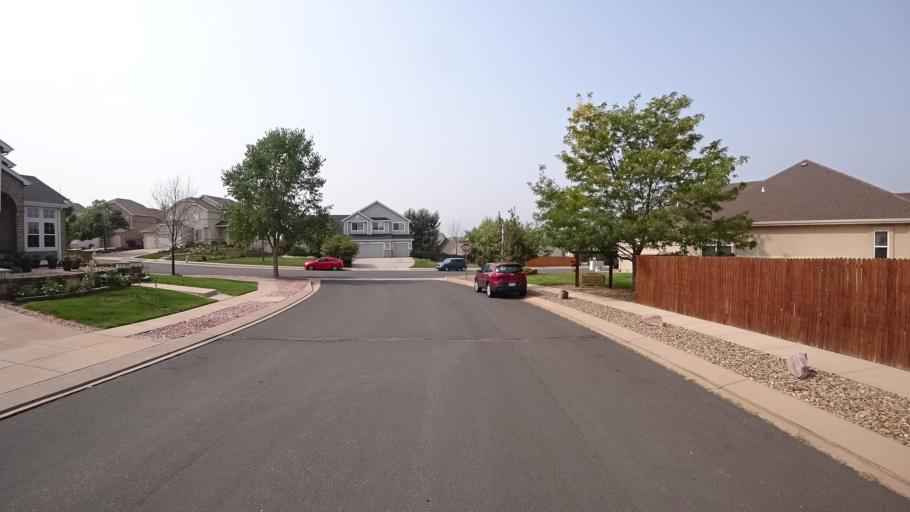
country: US
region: Colorado
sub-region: El Paso County
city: Cimarron Hills
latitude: 38.9249
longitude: -104.7442
